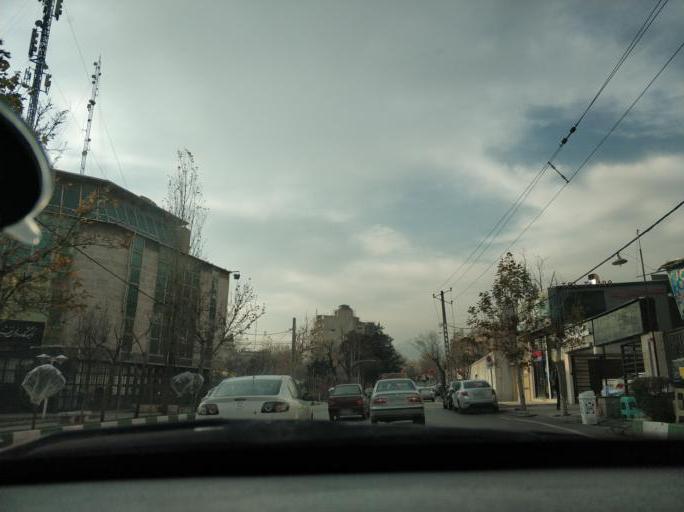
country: IR
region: Tehran
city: Tajrish
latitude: 35.8007
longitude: 51.4821
